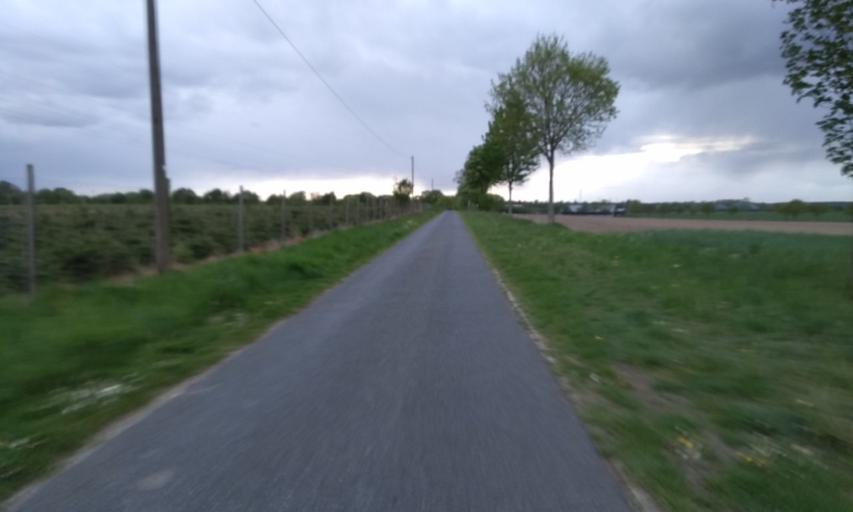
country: DE
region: Lower Saxony
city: Harsefeld
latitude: 53.4673
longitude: 9.4846
